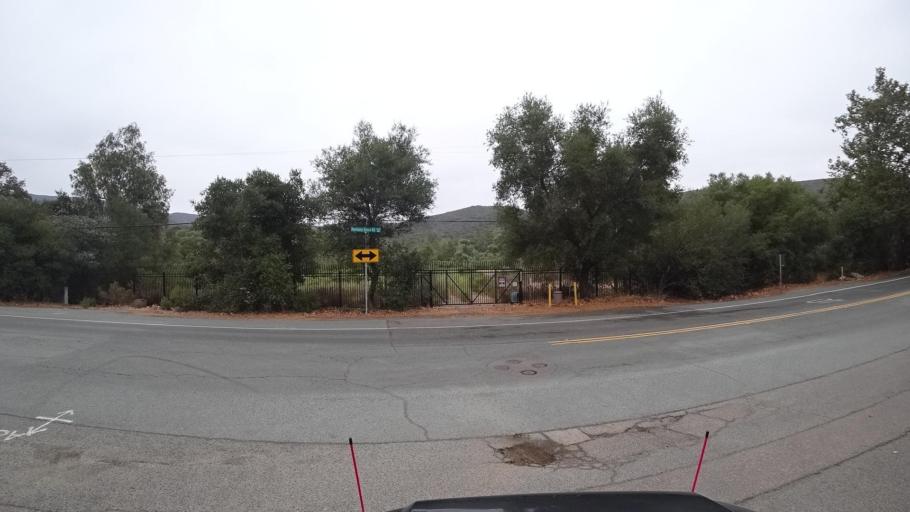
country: US
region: California
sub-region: San Diego County
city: Rancho Santa Fe
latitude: 33.0738
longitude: -117.1640
